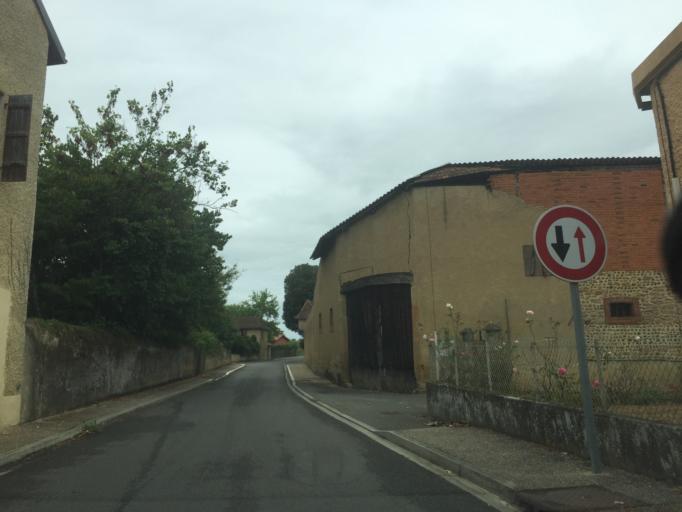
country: FR
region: Midi-Pyrenees
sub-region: Departement des Hautes-Pyrenees
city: Rabastens-de-Bigorre
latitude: 43.3758
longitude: 0.2125
